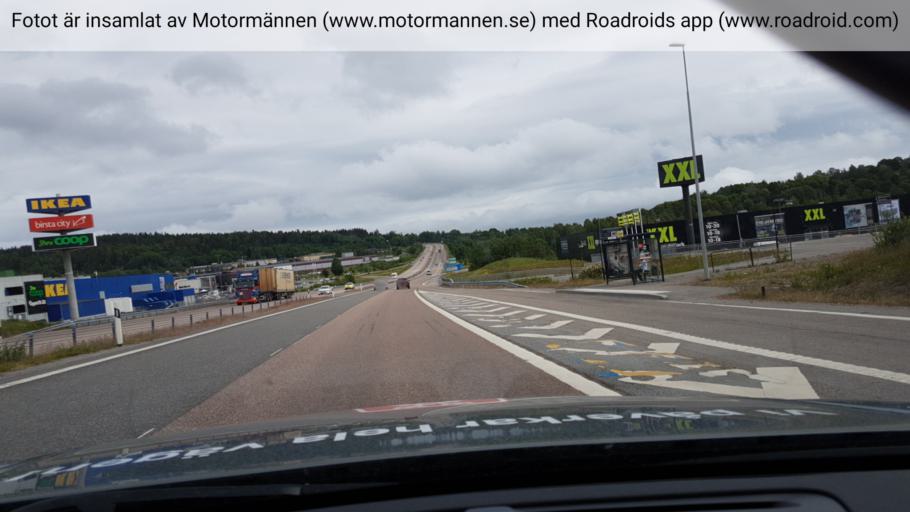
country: SE
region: Vaesternorrland
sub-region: Sundsvalls Kommun
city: Sundsbruk
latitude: 62.4429
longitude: 17.3370
